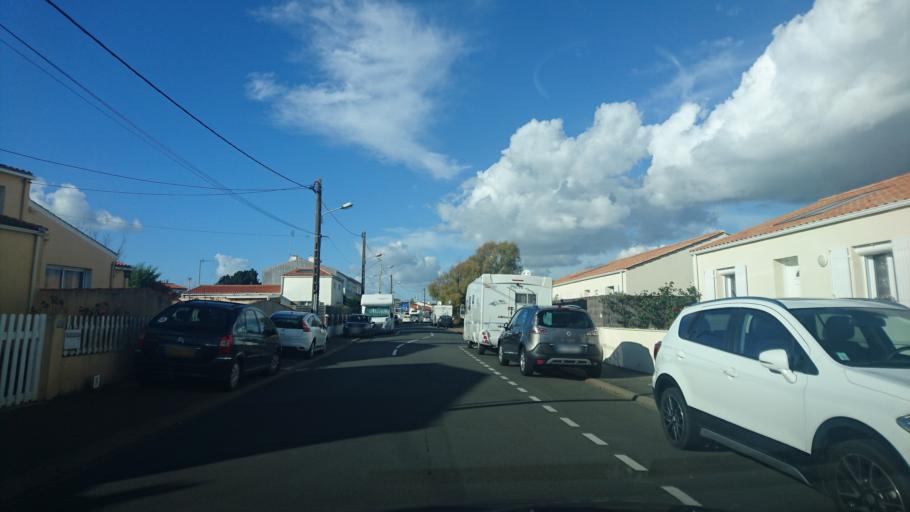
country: FR
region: Pays de la Loire
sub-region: Departement de la Vendee
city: Les Sables-d'Olonne
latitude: 46.5071
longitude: -1.8017
